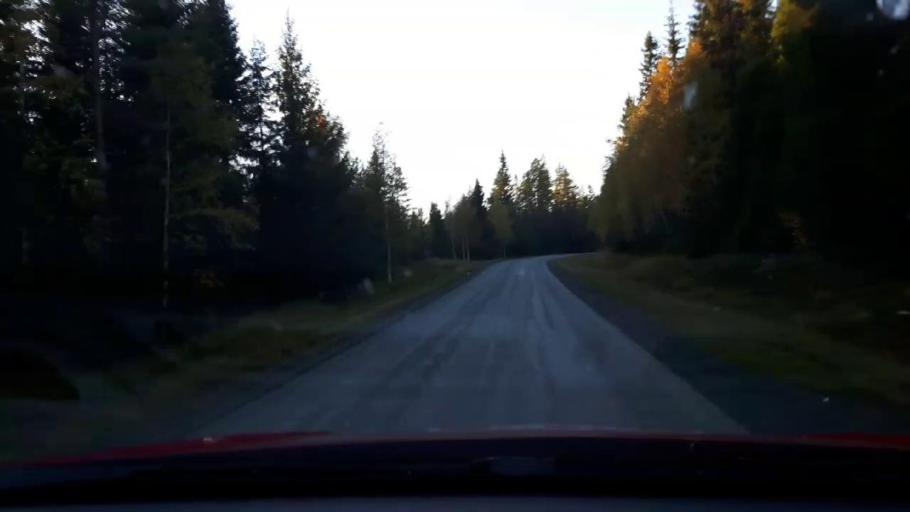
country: SE
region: Jaemtland
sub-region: Krokoms Kommun
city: Krokom
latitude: 63.4683
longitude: 14.3522
